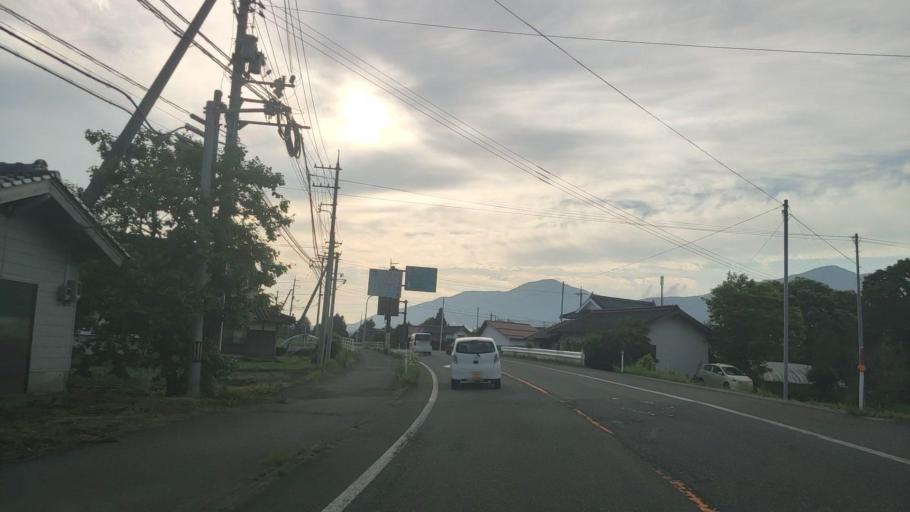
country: JP
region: Tottori
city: Kurayoshi
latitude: 35.2914
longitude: 133.7323
